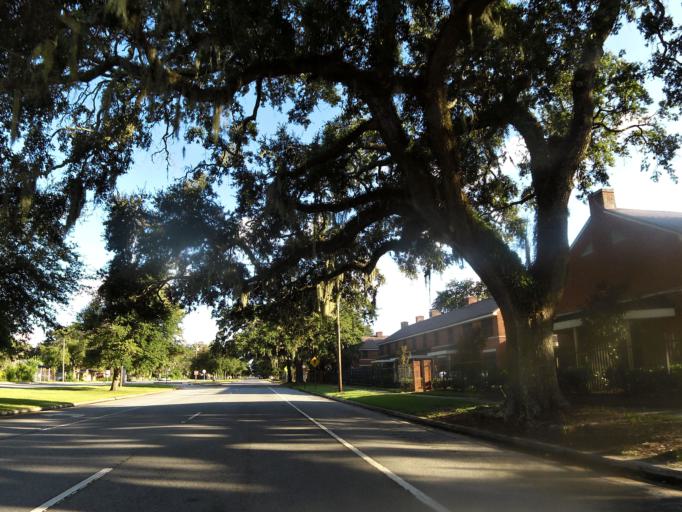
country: US
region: Georgia
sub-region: Glynn County
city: Brunswick
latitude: 31.1574
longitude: -81.4904
